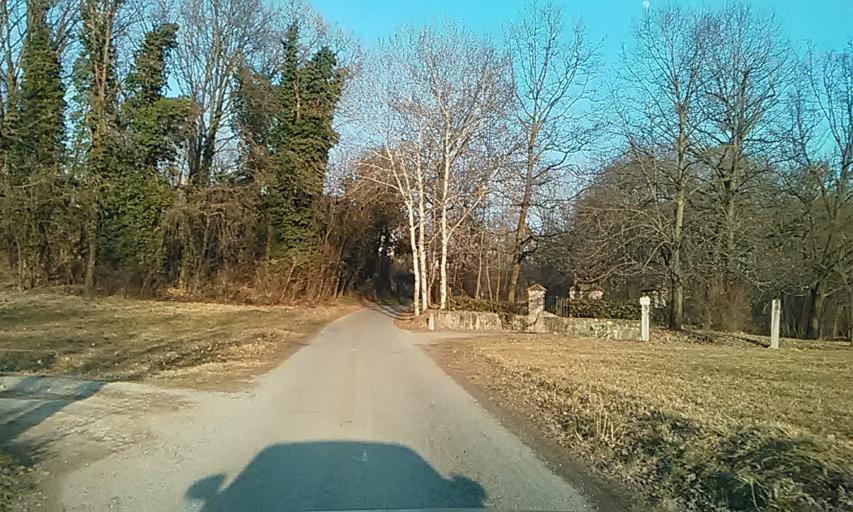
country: IT
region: Piedmont
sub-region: Provincia di Biella
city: Dorzano
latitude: 45.4156
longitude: 8.1062
